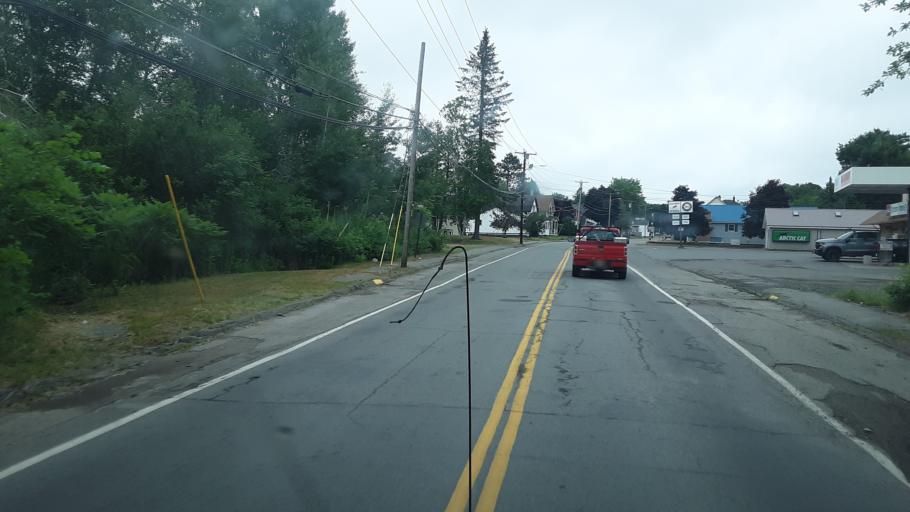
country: US
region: Maine
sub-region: Penobscot County
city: Millinocket
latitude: 45.6643
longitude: -68.7162
